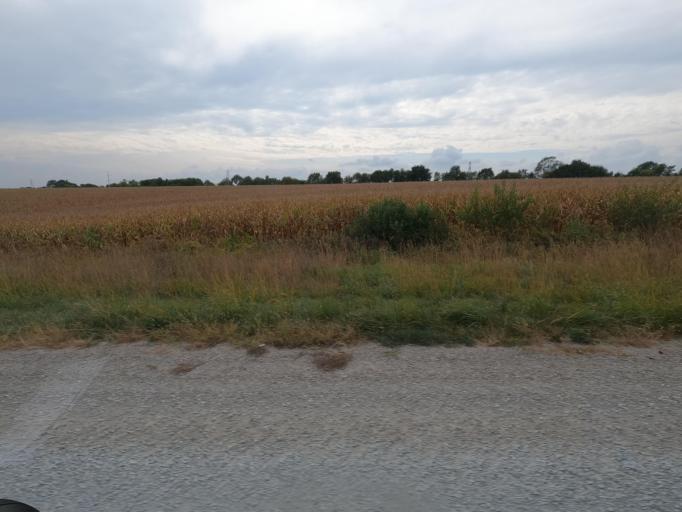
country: US
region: Iowa
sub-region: Marion County
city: Pella
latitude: 41.4235
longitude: -92.9685
